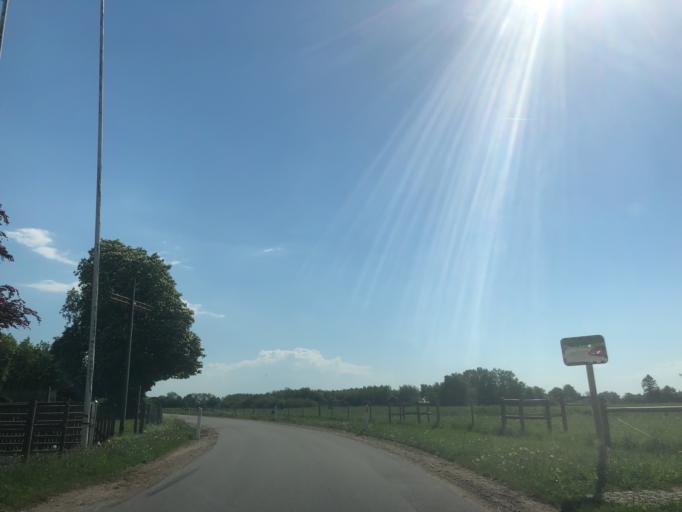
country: DK
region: Zealand
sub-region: Roskilde Kommune
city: Vindinge
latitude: 55.6160
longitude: 12.1137
